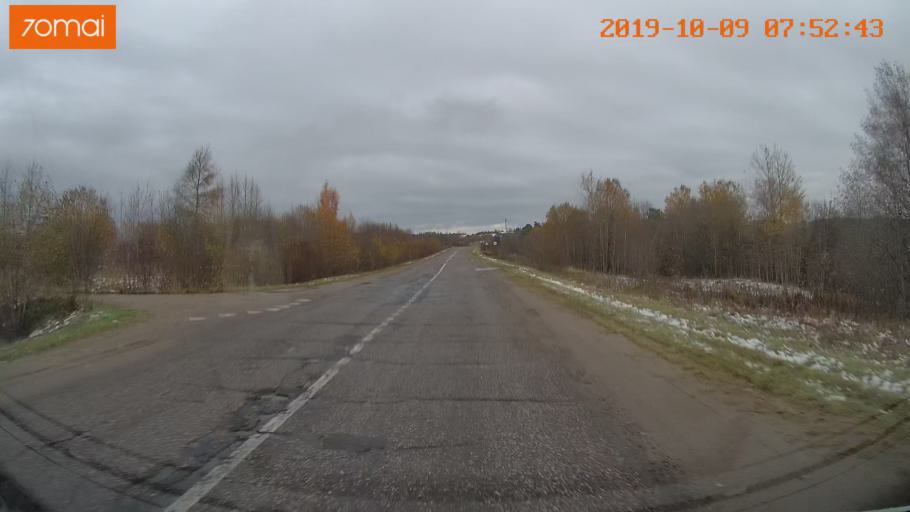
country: RU
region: Jaroslavl
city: Kukoboy
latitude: 58.6933
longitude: 39.8896
